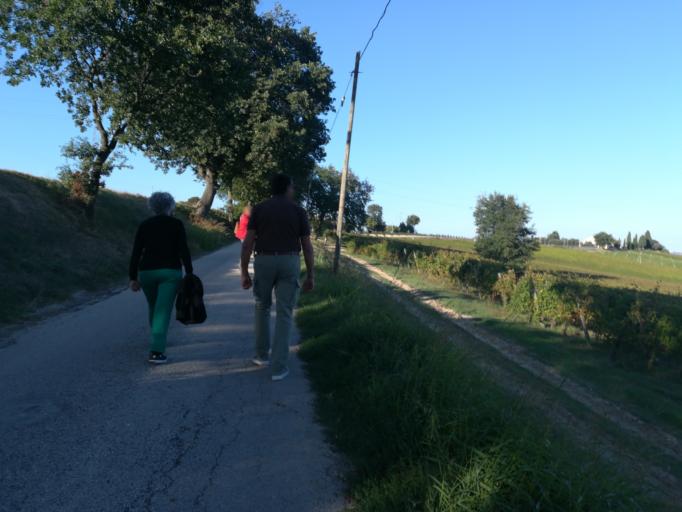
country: IT
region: The Marches
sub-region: Provincia di Macerata
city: Villa Potenza
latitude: 43.3322
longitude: 13.4159
